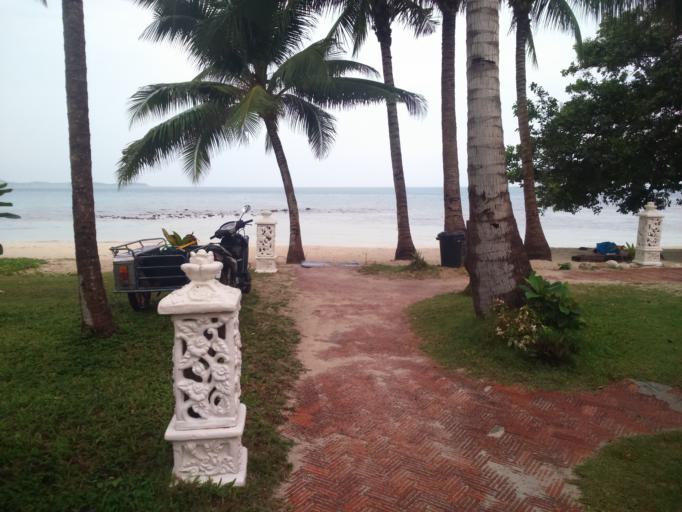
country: TH
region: Surat Thani
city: Ko Samui
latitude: 9.4770
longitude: 100.0671
